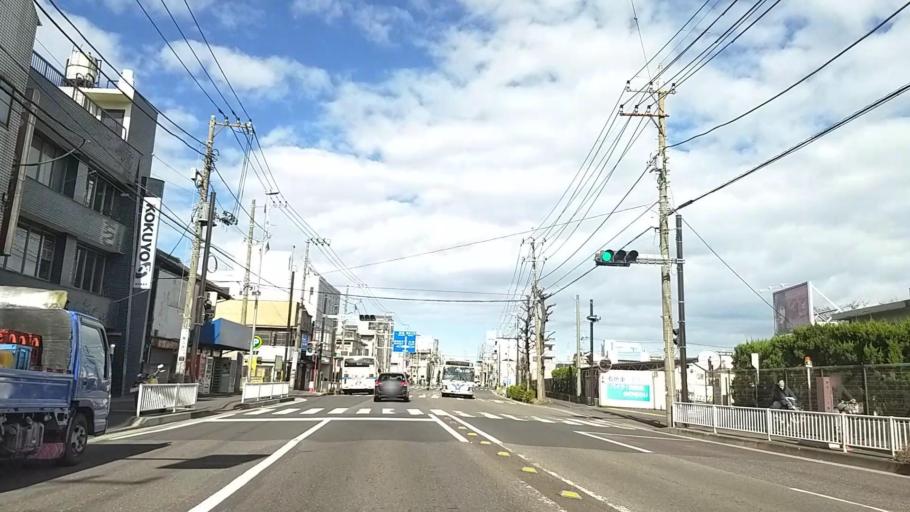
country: JP
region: Kanagawa
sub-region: Kawasaki-shi
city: Kawasaki
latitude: 35.5180
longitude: 139.6731
